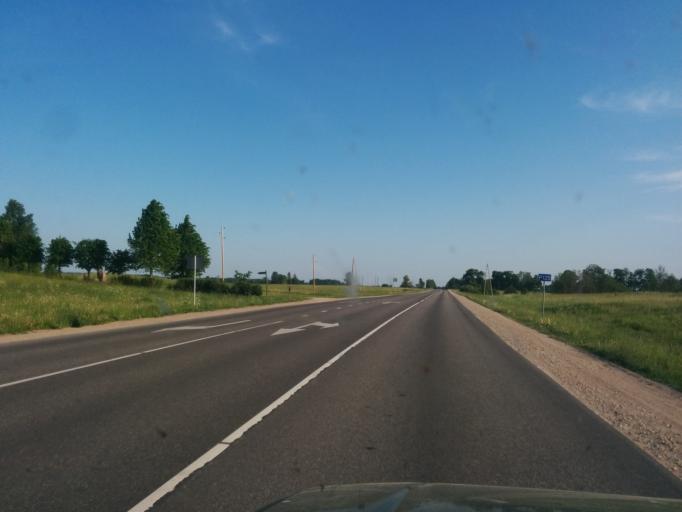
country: LV
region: Talsu Rajons
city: Talsi
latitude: 57.2869
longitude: 22.5731
